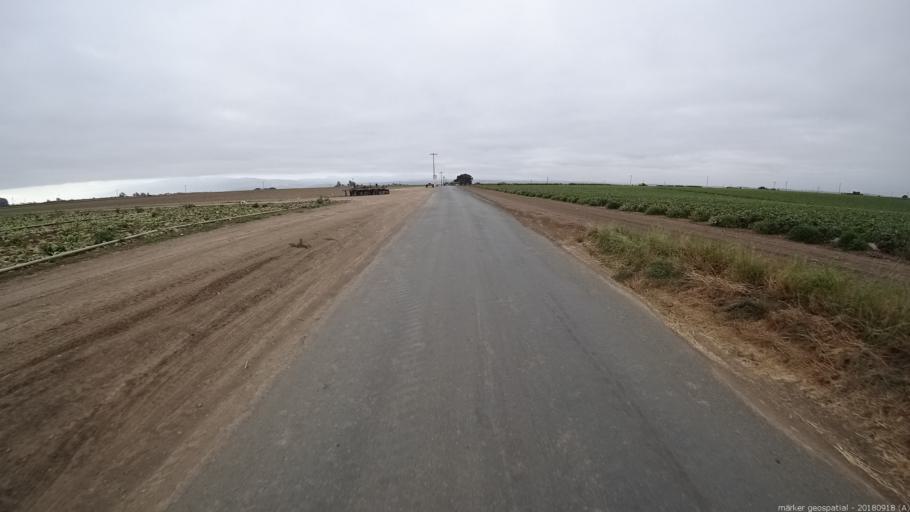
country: US
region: California
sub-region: Monterey County
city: Boronda
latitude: 36.7368
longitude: -121.6948
